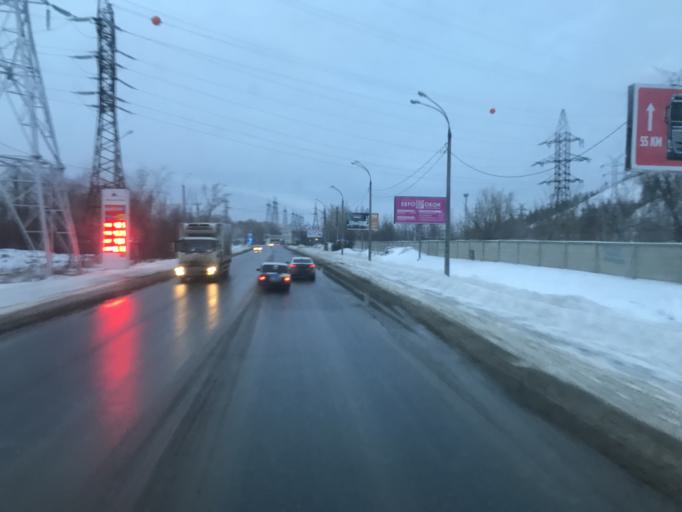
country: RU
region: Samara
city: Zhigulevsk
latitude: 53.4168
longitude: 49.4820
